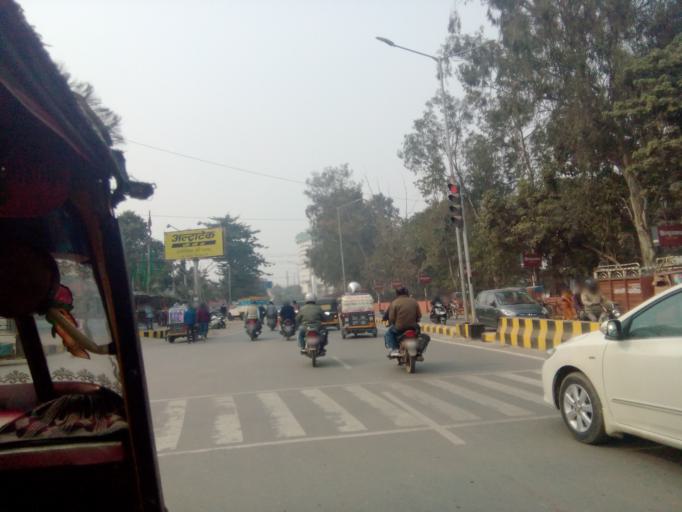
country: IN
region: Bihar
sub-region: Patna
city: Patna
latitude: 25.6155
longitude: 85.1444
